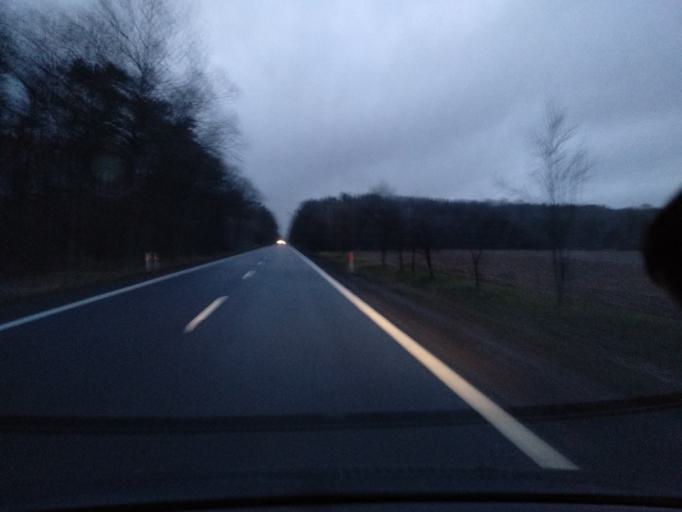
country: PL
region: Lower Silesian Voivodeship
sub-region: Powiat sredzki
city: Ciechow
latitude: 51.1755
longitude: 16.5355
